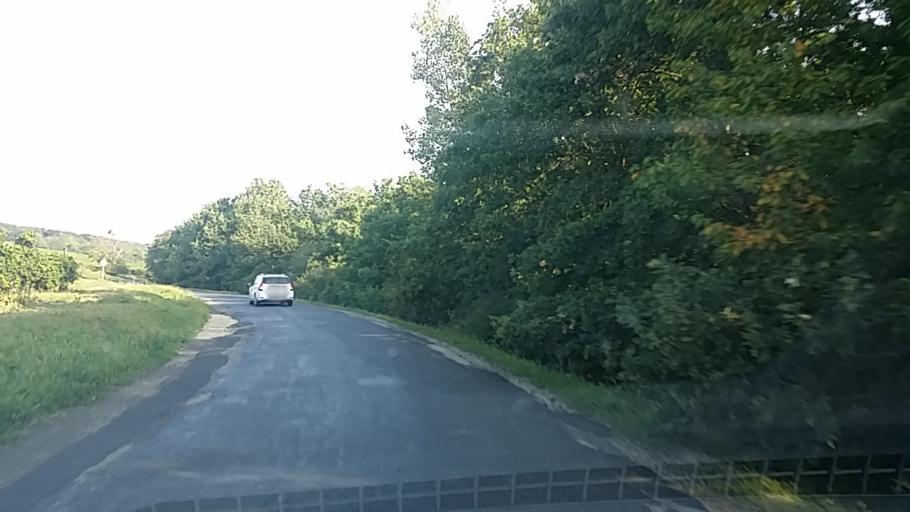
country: HU
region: Gyor-Moson-Sopron
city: Fertorakos
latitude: 47.6939
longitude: 16.6627
